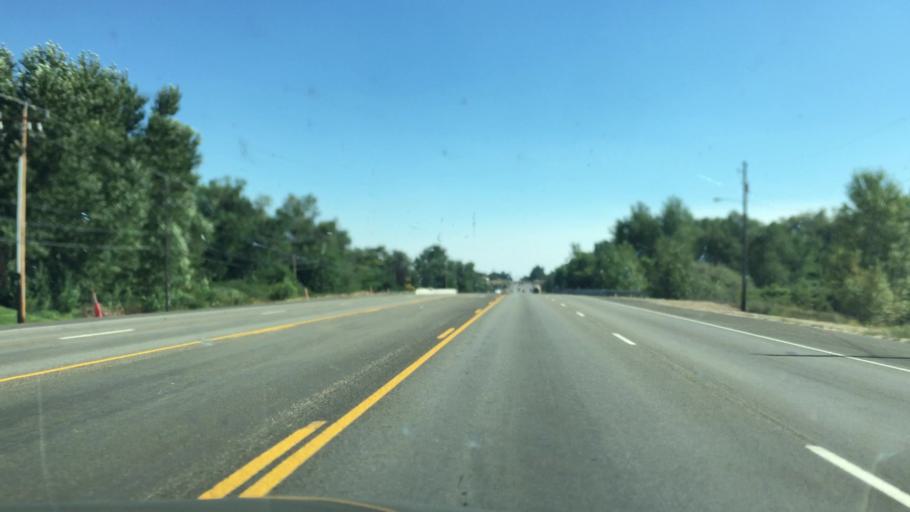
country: US
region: Idaho
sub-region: Ada County
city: Eagle
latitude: 43.6769
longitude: -116.3542
